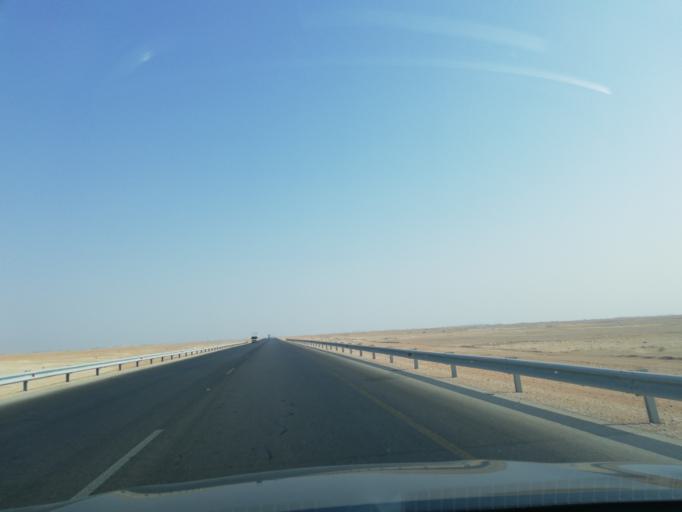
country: OM
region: Zufar
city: Salalah
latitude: 17.7612
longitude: 54.0174
